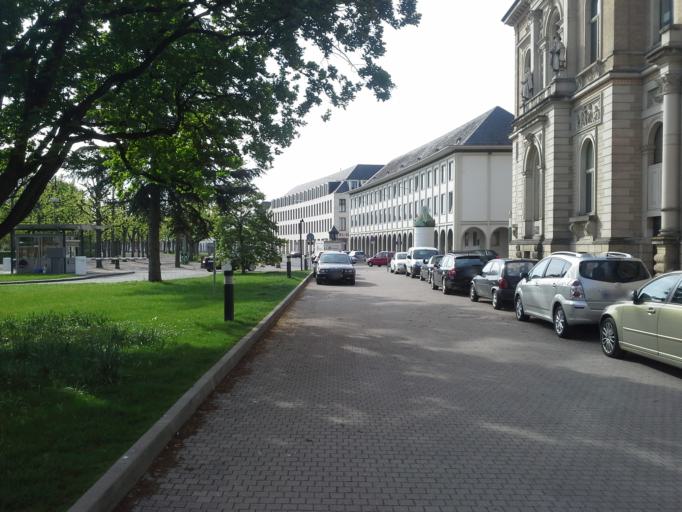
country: DE
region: Baden-Wuerttemberg
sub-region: Karlsruhe Region
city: Karlsruhe
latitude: 49.0123
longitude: 8.4002
